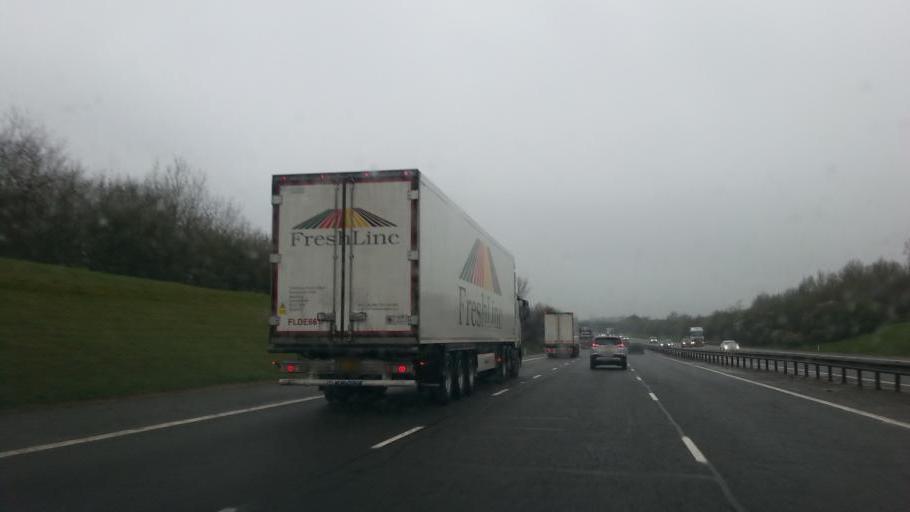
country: GB
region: England
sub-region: Warwickshire
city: Harbury
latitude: 52.2001
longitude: -1.4714
